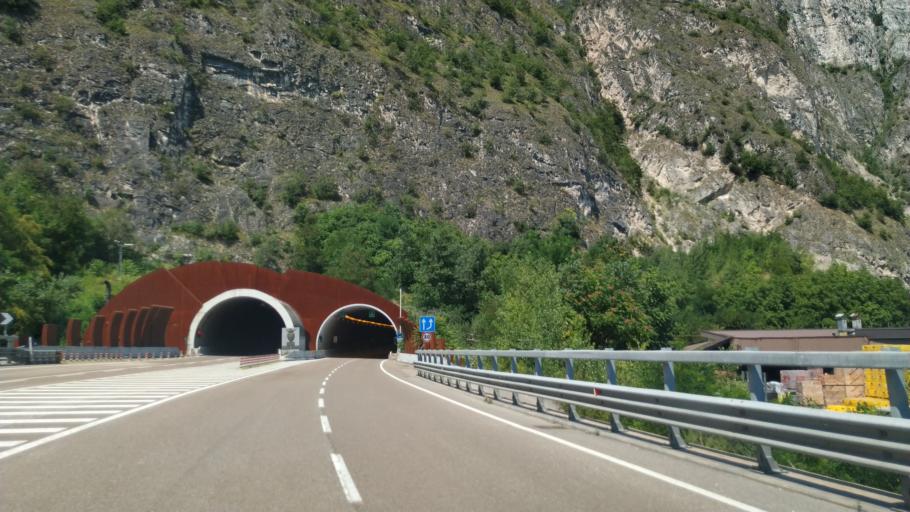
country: IT
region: Trentino-Alto Adige
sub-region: Provincia di Trento
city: Mezzolombardo
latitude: 46.1917
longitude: 11.0969
